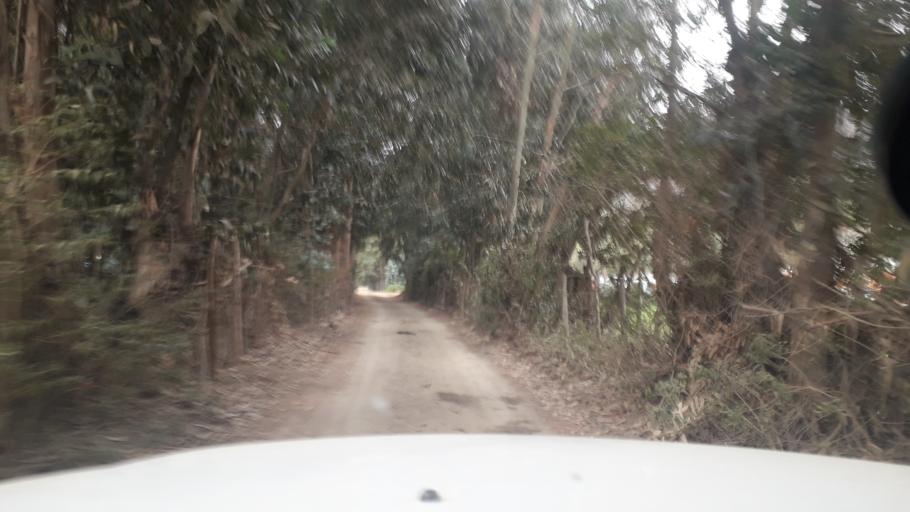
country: CL
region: Valparaiso
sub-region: Provincia de Valparaiso
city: Valparaiso
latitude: -33.1178
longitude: -71.6355
